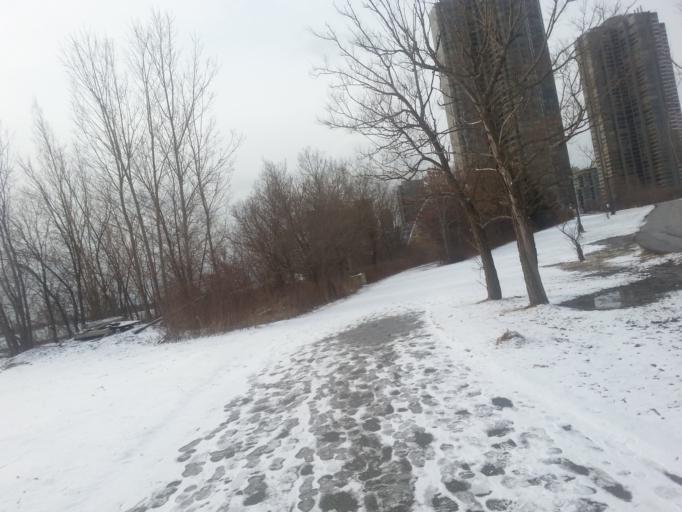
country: CA
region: Ontario
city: Toronto
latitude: 43.6329
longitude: -79.4694
